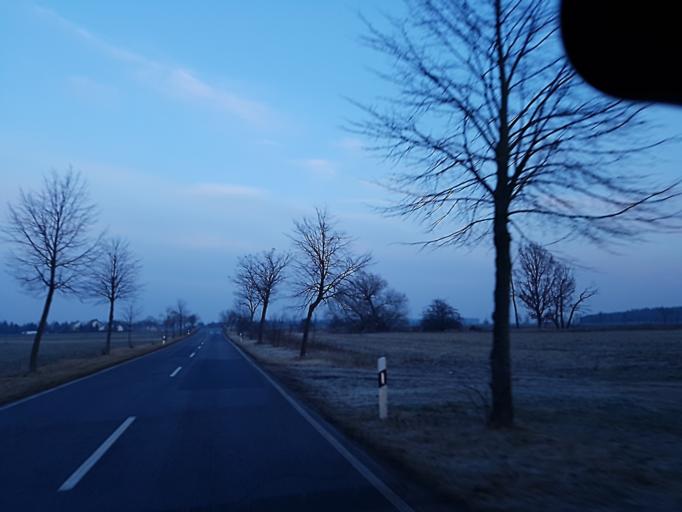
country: DE
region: Saxony-Anhalt
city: Holzdorf
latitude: 51.7792
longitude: 13.0744
